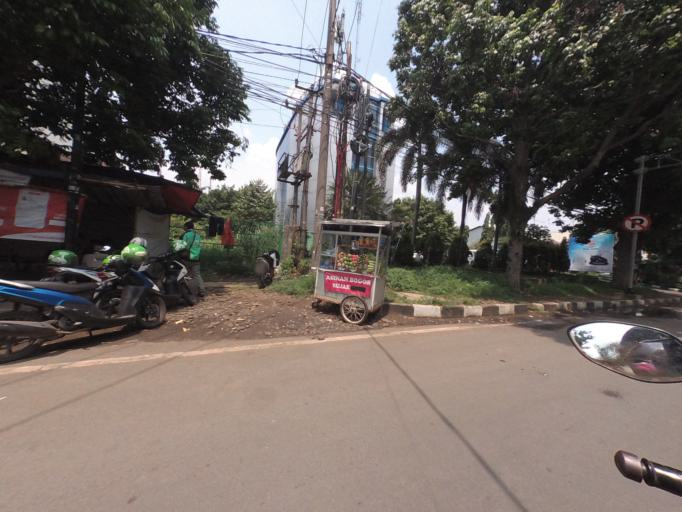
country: ID
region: West Java
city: Bogor
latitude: -6.5576
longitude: 106.7731
